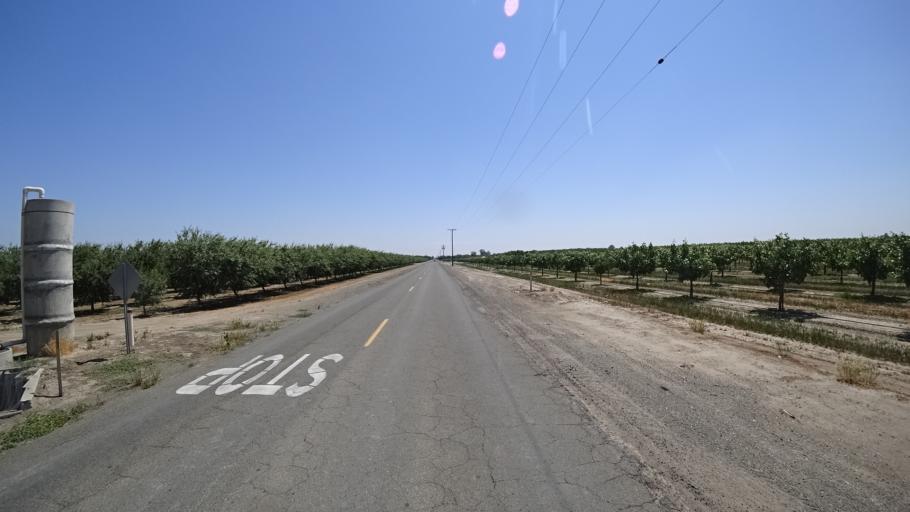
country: US
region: California
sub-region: Kings County
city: Armona
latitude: 36.3571
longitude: -119.7074
